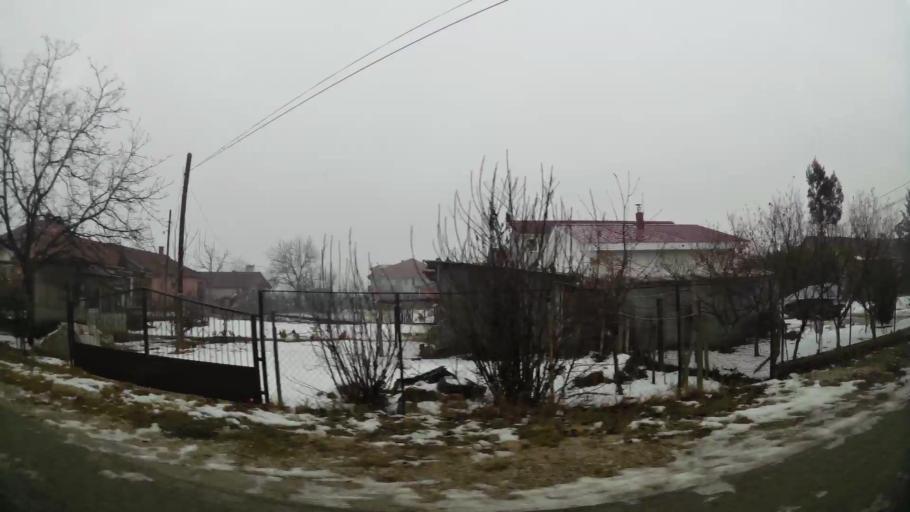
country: MK
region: Petrovec
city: Petrovec
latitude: 41.9322
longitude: 21.6236
